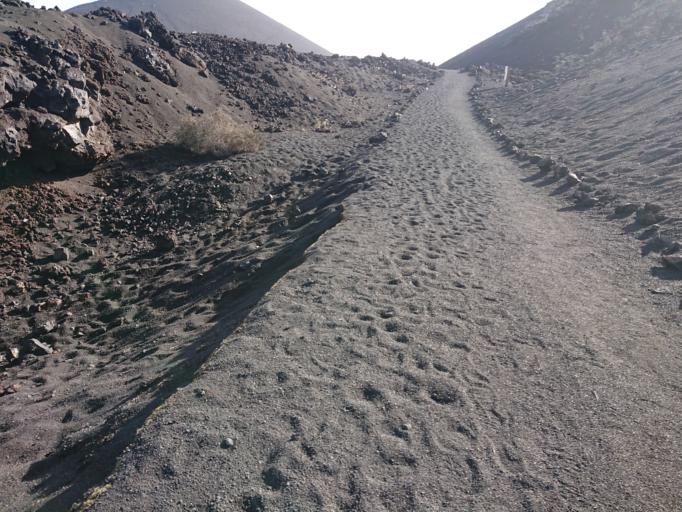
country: ES
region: Canary Islands
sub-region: Provincia de Las Palmas
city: Tias
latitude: 28.9932
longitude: -13.6922
